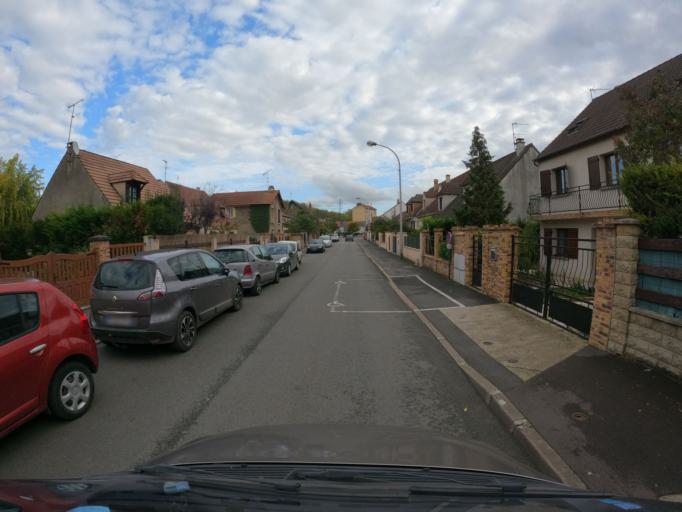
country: FR
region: Ile-de-France
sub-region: Departement de Seine-et-Marne
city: Chelles
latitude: 48.8834
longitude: 2.5846
